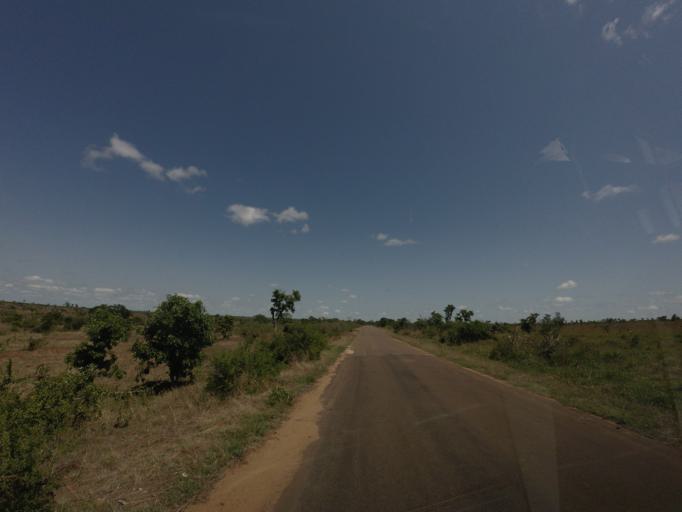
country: ZA
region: Mpumalanga
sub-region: Ehlanzeni District
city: Komatipoort
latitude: -24.9936
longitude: 31.9092
